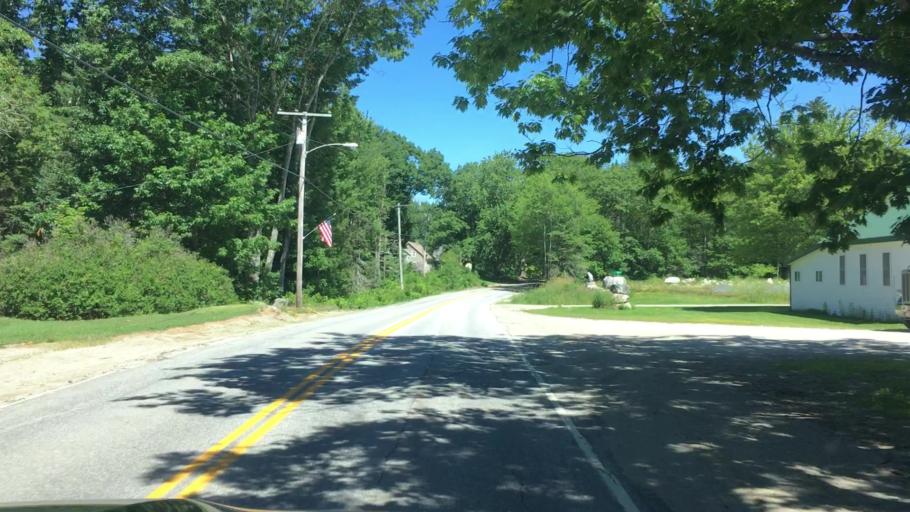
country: US
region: Maine
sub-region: Hancock County
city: Penobscot
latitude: 44.4574
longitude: -68.7045
